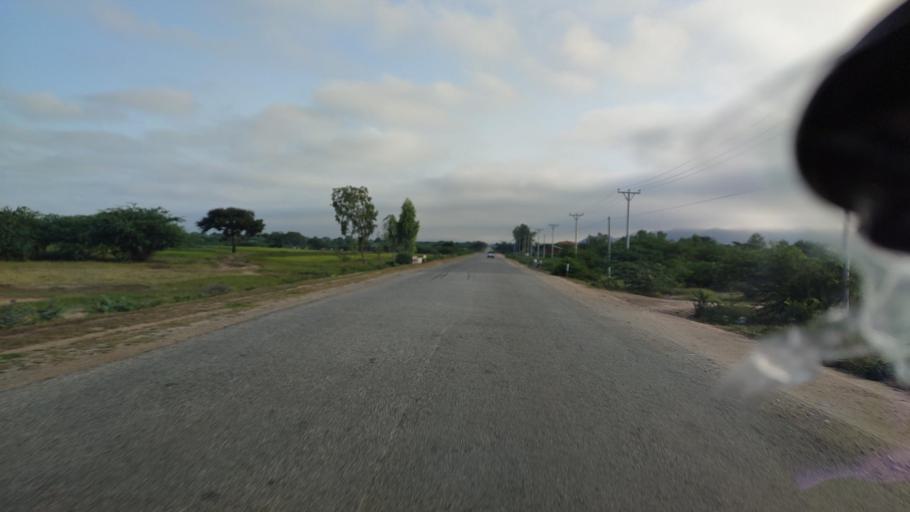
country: MM
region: Mandalay
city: Yamethin
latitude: 20.7025
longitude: 96.1732
